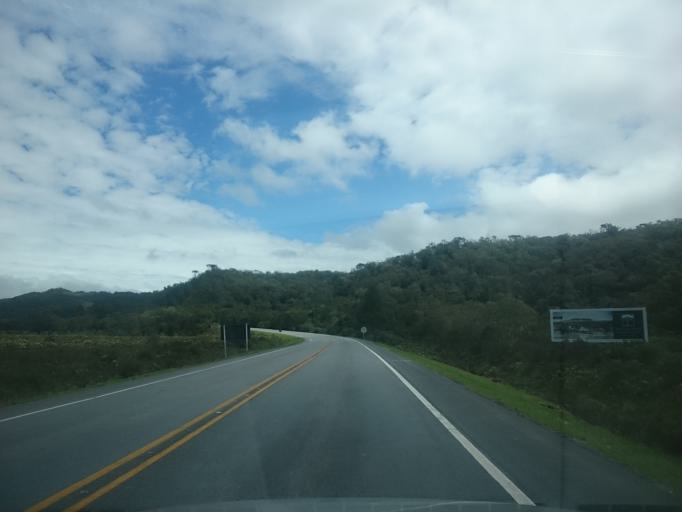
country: BR
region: Santa Catarina
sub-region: Anitapolis
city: Anitapolis
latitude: -27.6875
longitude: -49.0360
